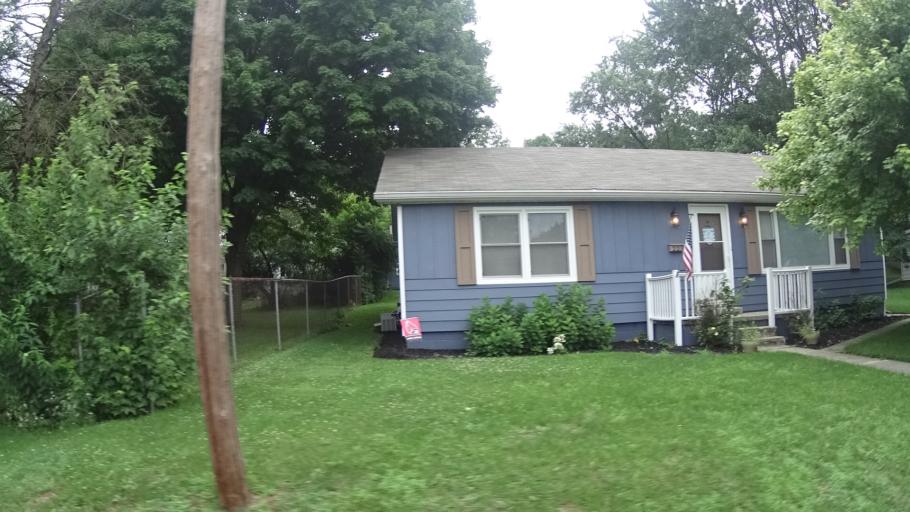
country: US
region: Indiana
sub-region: Madison County
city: Pendleton
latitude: 40.0003
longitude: -85.7530
